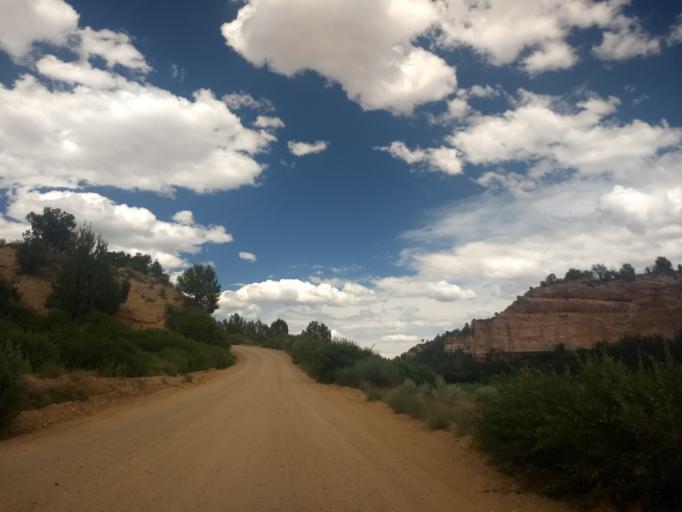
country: US
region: Utah
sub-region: Kane County
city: Kanab
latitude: 37.1458
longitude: -112.5403
